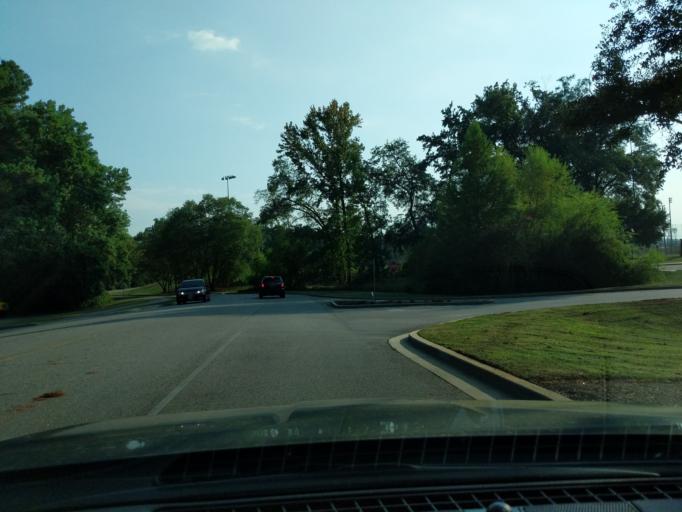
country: US
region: South Carolina
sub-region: Aiken County
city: North Augusta
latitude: 33.5026
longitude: -81.9812
